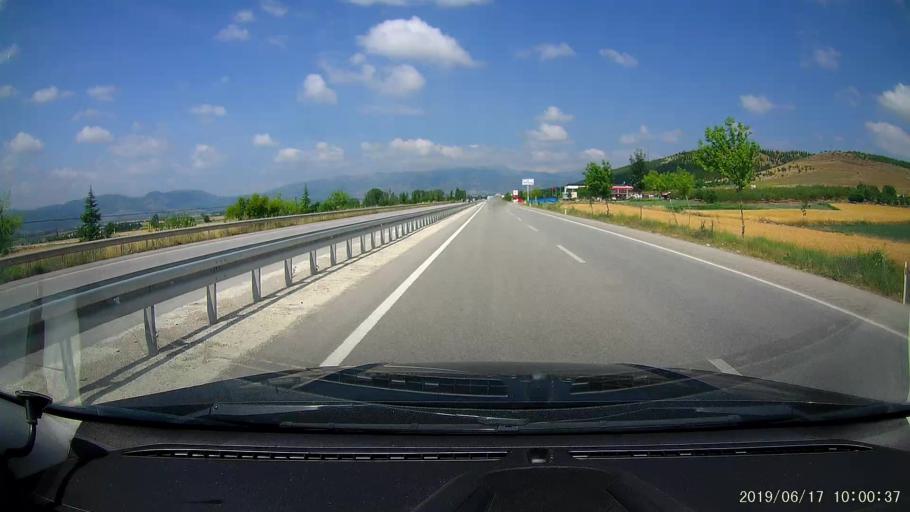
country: TR
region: Amasya
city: Gumushacikoy
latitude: 40.8661
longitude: 35.2837
